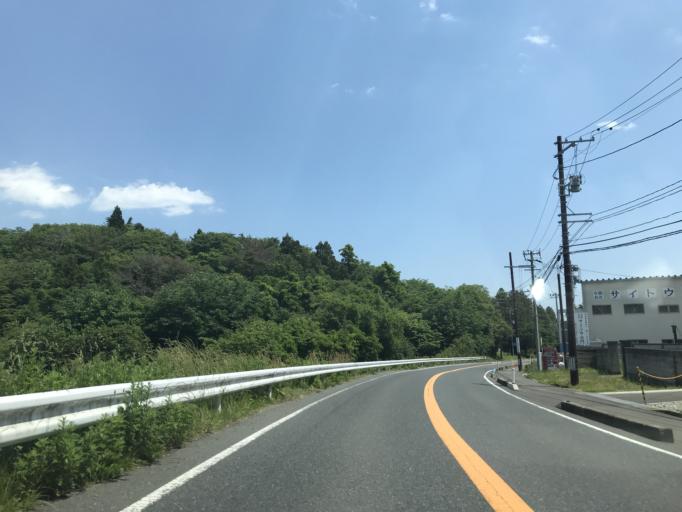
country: JP
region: Miyagi
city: Matsushima
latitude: 38.3870
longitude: 141.1124
